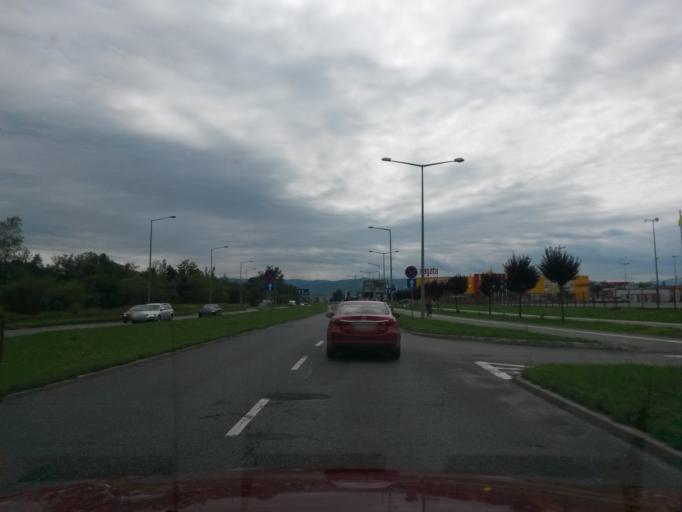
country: PL
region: Lesser Poland Voivodeship
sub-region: Powiat nowosadecki
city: Nowy Sacz
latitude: 49.6041
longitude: 20.7287
